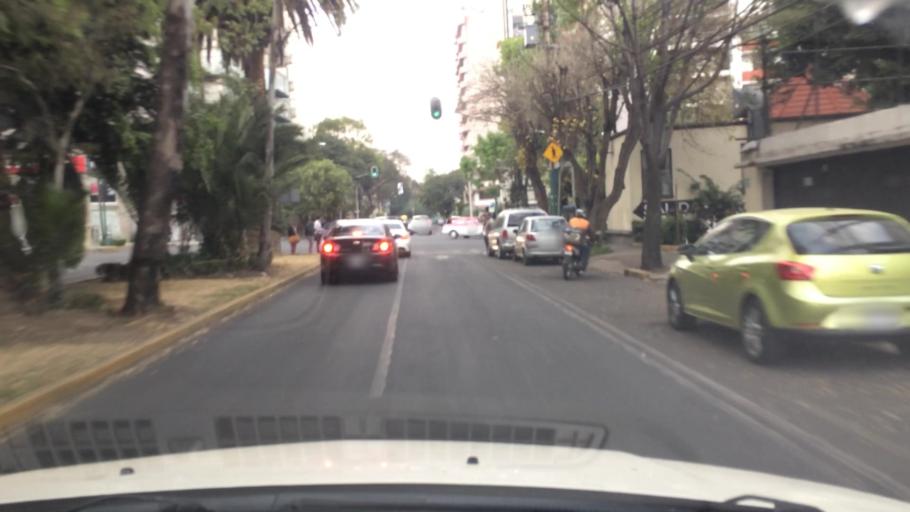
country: MX
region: Mexico City
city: Alvaro Obregon
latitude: 19.3613
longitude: -99.1850
